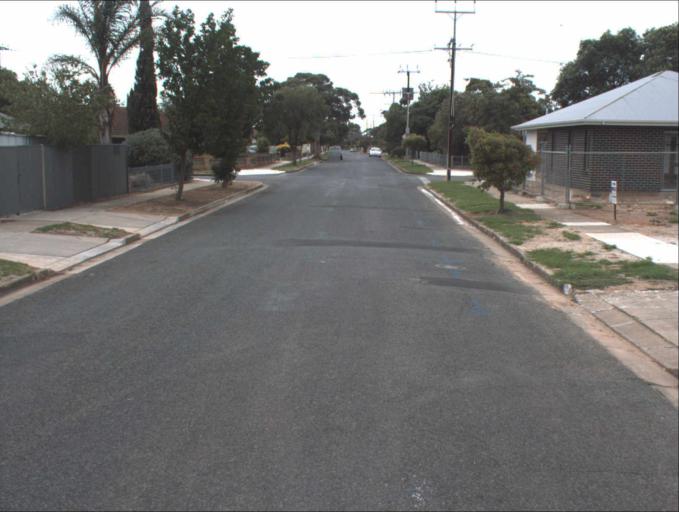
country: AU
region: South Australia
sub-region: Port Adelaide Enfield
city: Enfield
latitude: -34.8549
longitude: 138.6190
